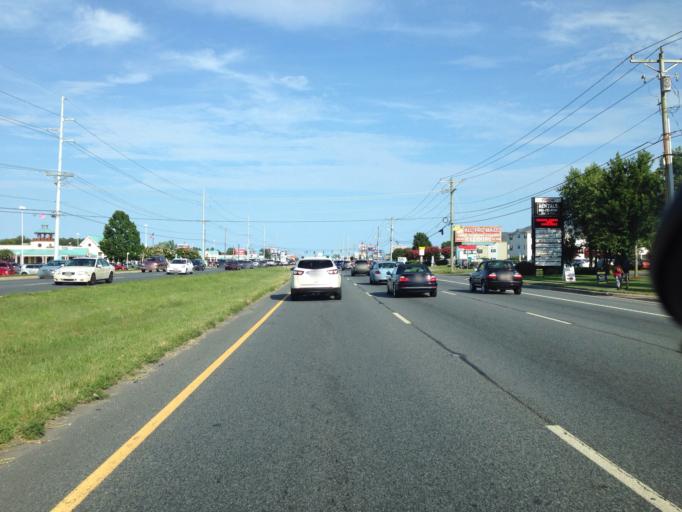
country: US
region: Delaware
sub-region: Sussex County
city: Rehoboth Beach
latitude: 38.7192
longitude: -75.1161
